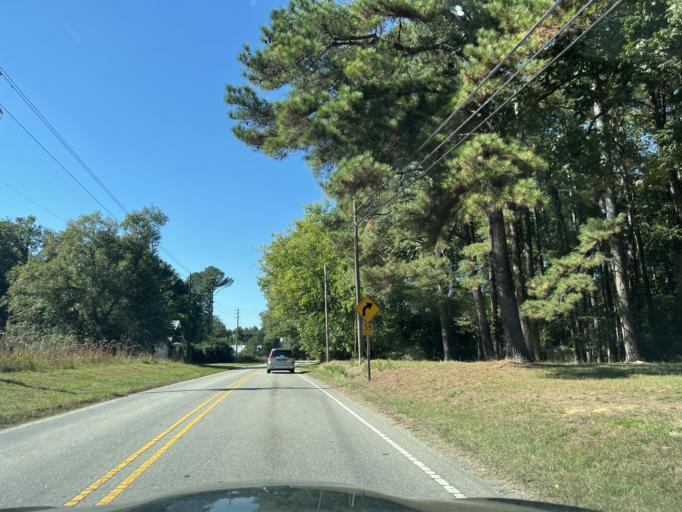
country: US
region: North Carolina
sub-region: Wake County
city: Garner
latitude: 35.6927
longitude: -78.5525
